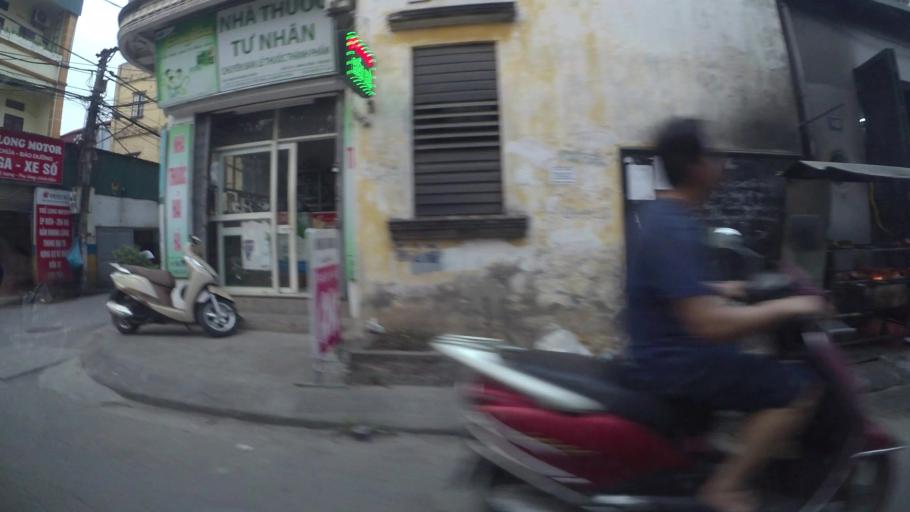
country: VN
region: Ha Noi
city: Hoan Kiem
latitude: 21.0566
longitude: 105.8958
